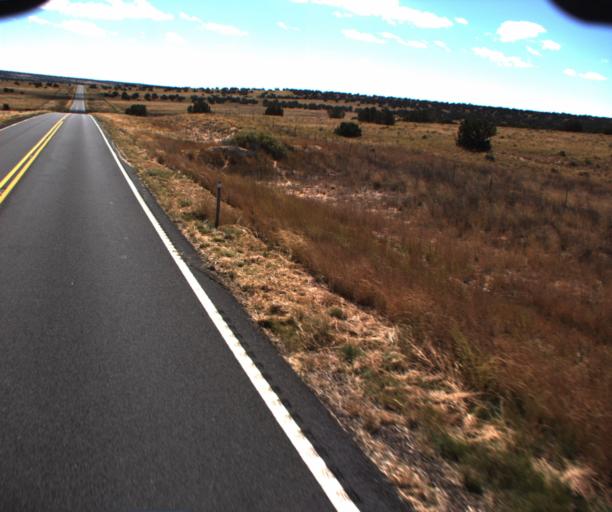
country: US
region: Arizona
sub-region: Apache County
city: Houck
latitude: 35.0183
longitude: -109.2398
